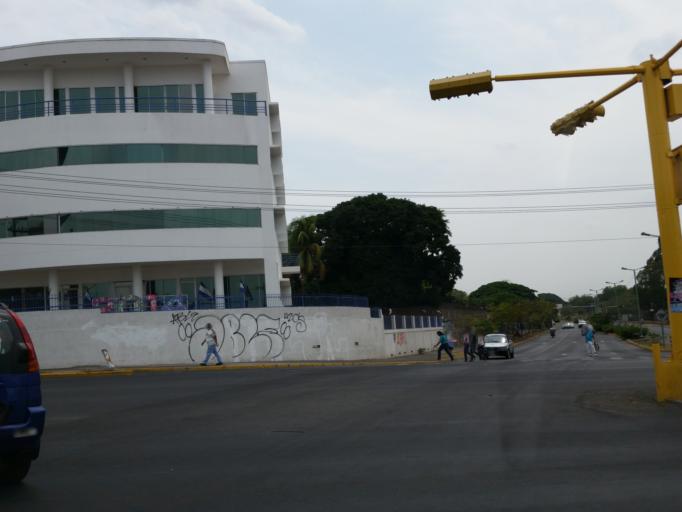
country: NI
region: Managua
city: Managua
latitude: 12.1233
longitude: -86.2641
